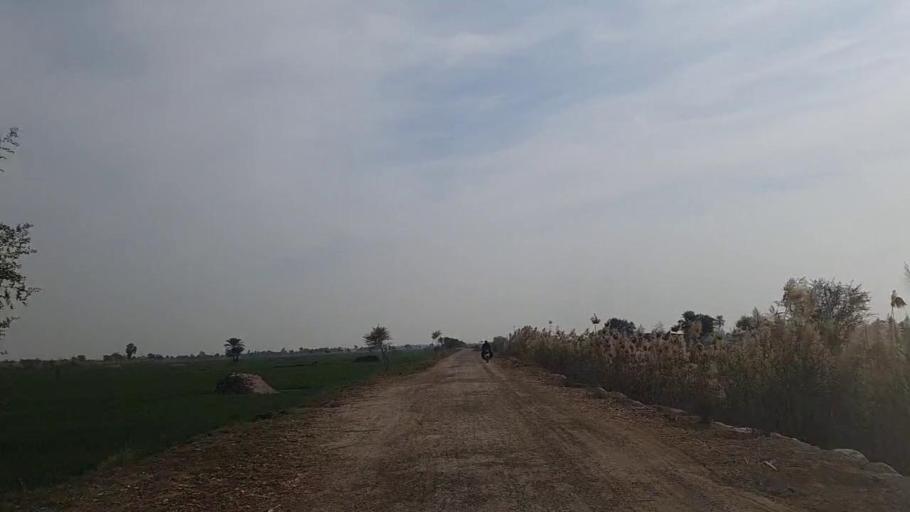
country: PK
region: Sindh
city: Daur
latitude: 26.4465
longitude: 68.4186
